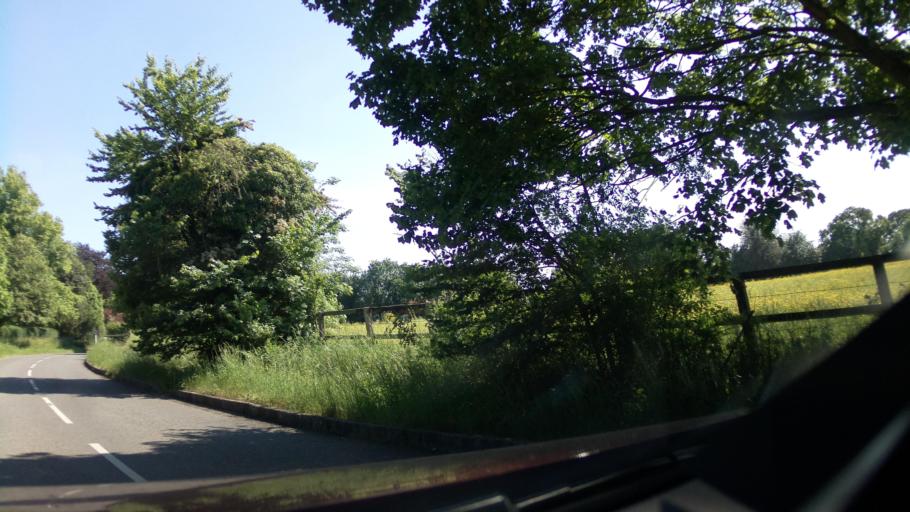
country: GB
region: England
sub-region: Hampshire
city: Abbotts Ann
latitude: 51.2344
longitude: -1.5631
